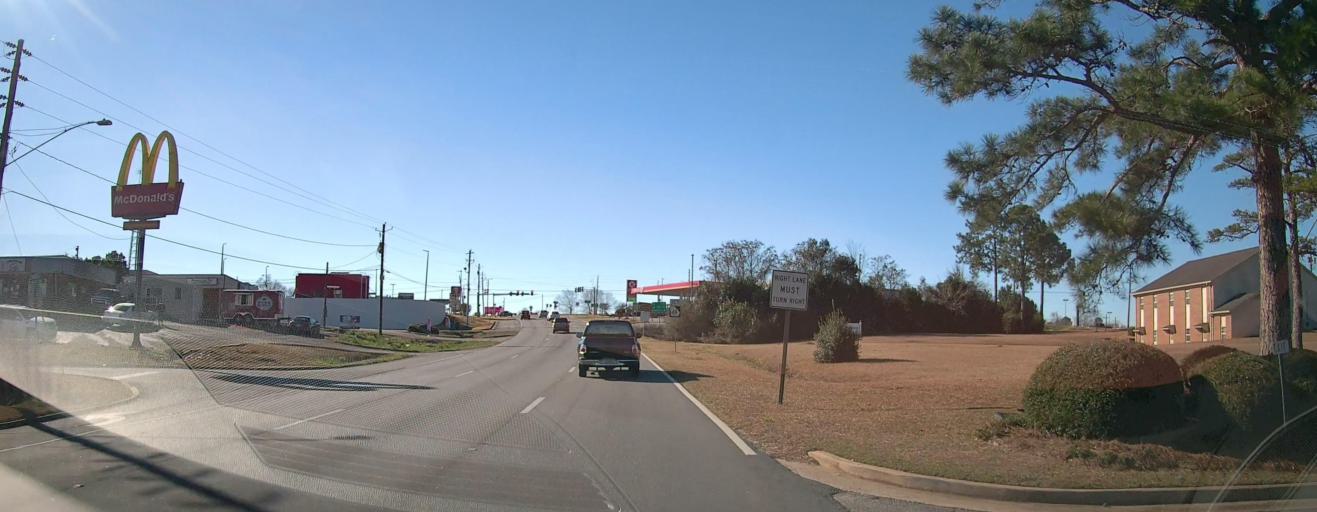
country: US
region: Georgia
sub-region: Sumter County
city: Americus
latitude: 32.0729
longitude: -84.2158
